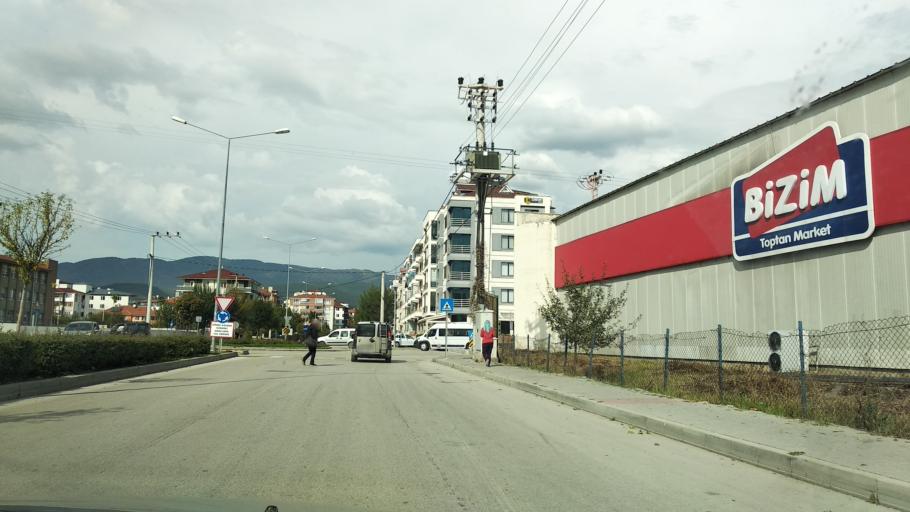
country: TR
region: Bolu
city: Bolu
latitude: 40.7268
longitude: 31.5880
